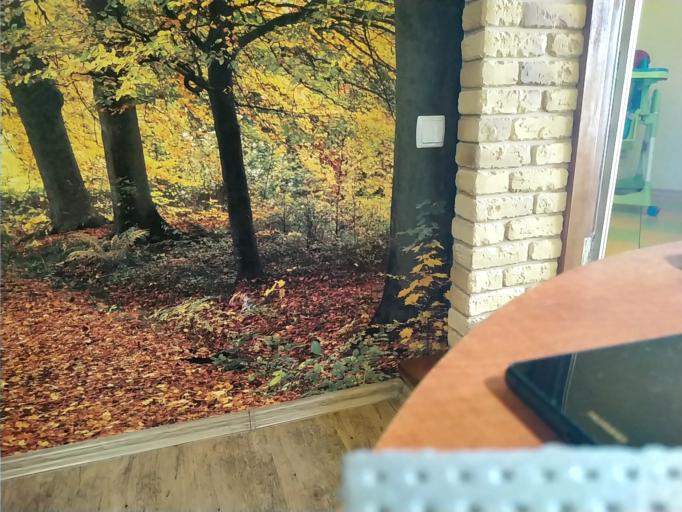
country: RU
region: Kaluga
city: Kondrovo
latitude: 54.7976
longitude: 35.9180
